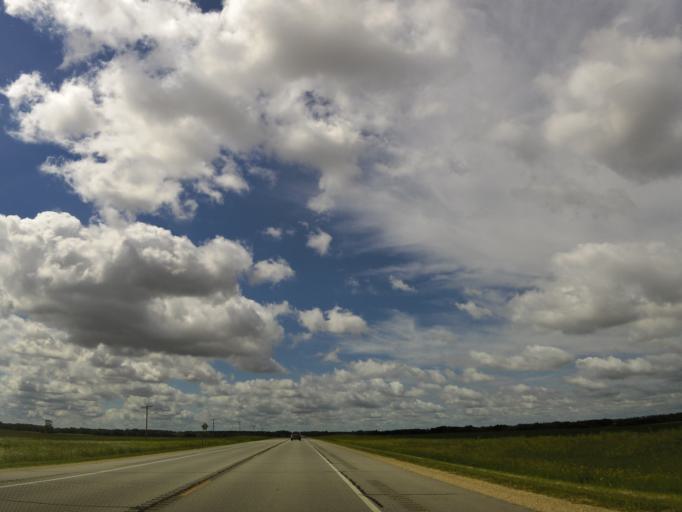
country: US
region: Minnesota
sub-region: Olmsted County
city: Stewartville
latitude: 43.7601
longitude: -92.4791
